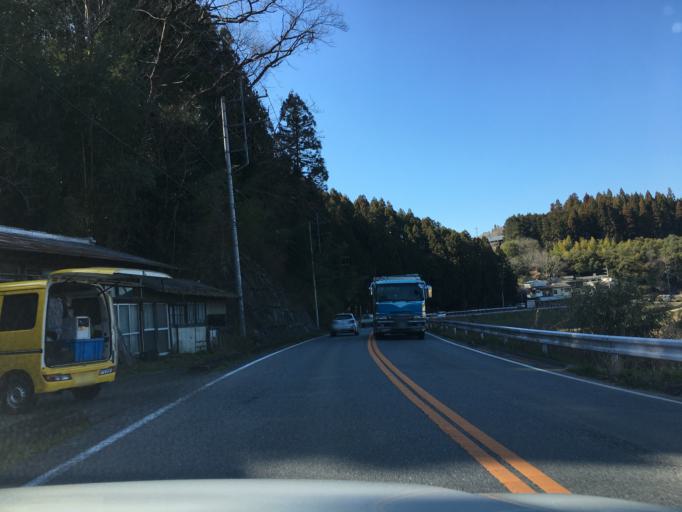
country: JP
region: Tochigi
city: Motegi
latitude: 36.5559
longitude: 140.2394
